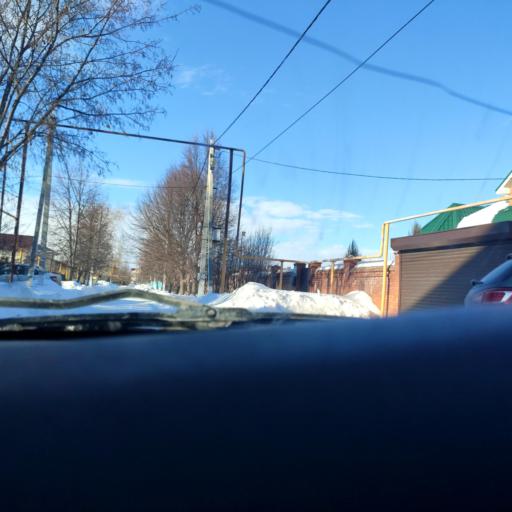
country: RU
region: Samara
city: Podstepki
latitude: 53.5142
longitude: 49.1563
